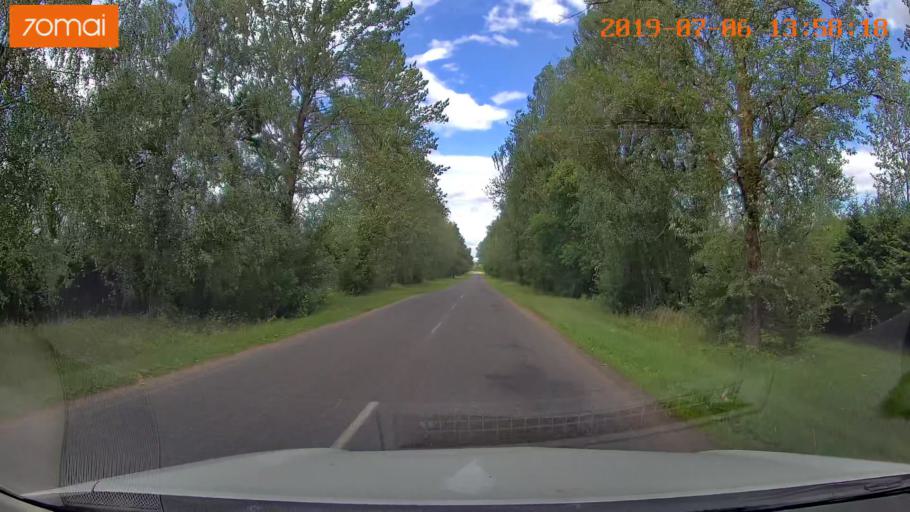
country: BY
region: Minsk
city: Ivyanyets
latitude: 53.7825
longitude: 26.8086
